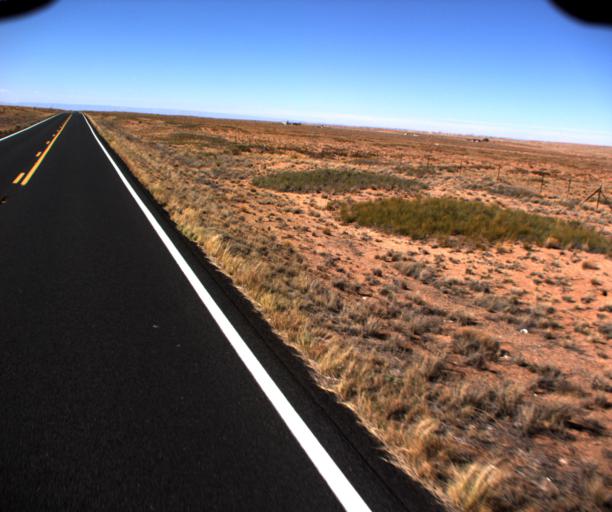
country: US
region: Arizona
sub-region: Coconino County
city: Tuba City
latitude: 36.0170
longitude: -111.1021
